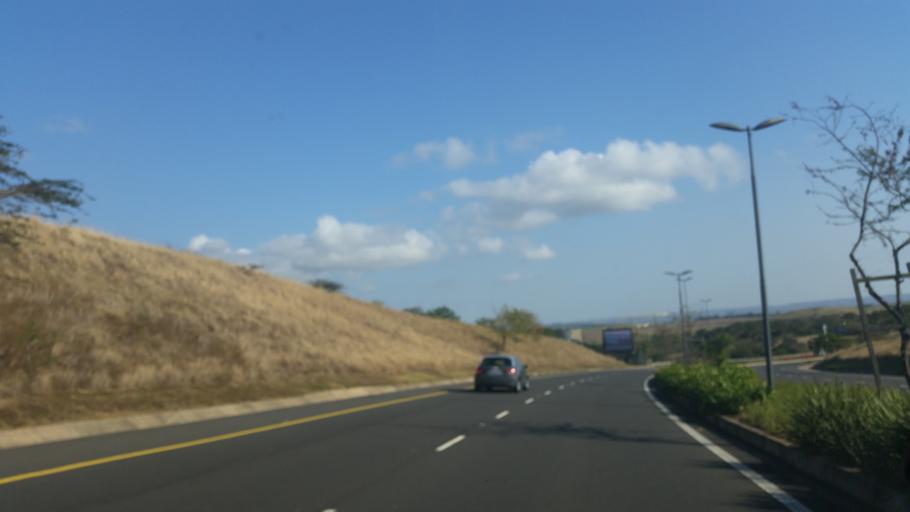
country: ZA
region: KwaZulu-Natal
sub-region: iLembe District Municipality
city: Ballitoville
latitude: -29.6280
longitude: 31.1047
